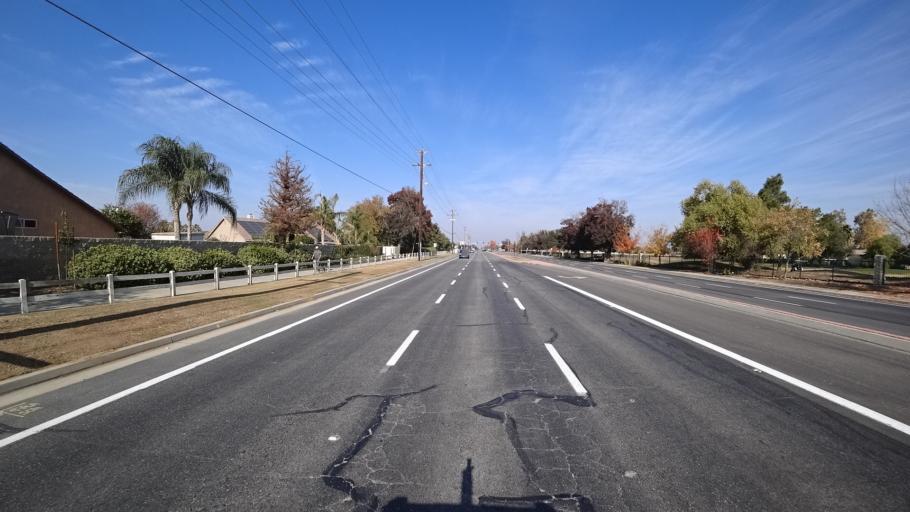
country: US
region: California
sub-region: Kern County
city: Greenacres
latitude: 35.4080
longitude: -119.1101
